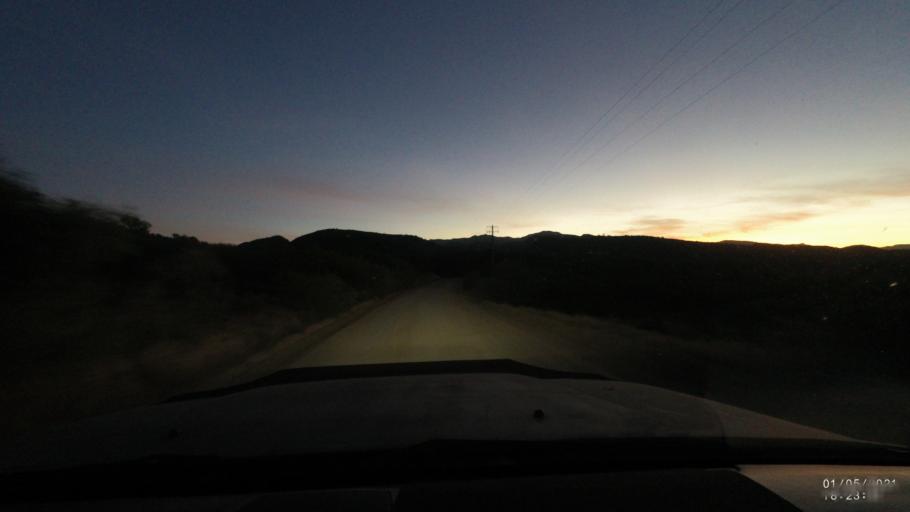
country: BO
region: Cochabamba
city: Capinota
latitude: -17.6587
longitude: -66.2400
